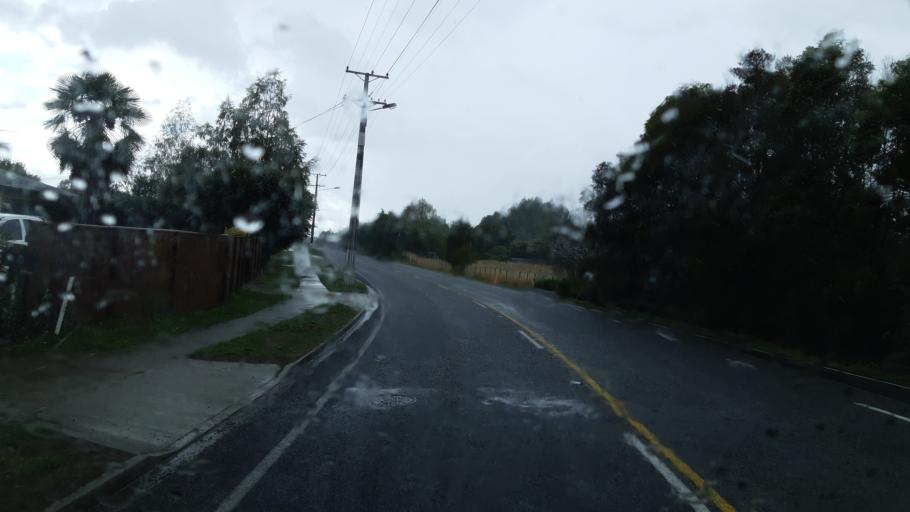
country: NZ
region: Tasman
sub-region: Tasman District
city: Wakefield
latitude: -41.4039
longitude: 173.0526
